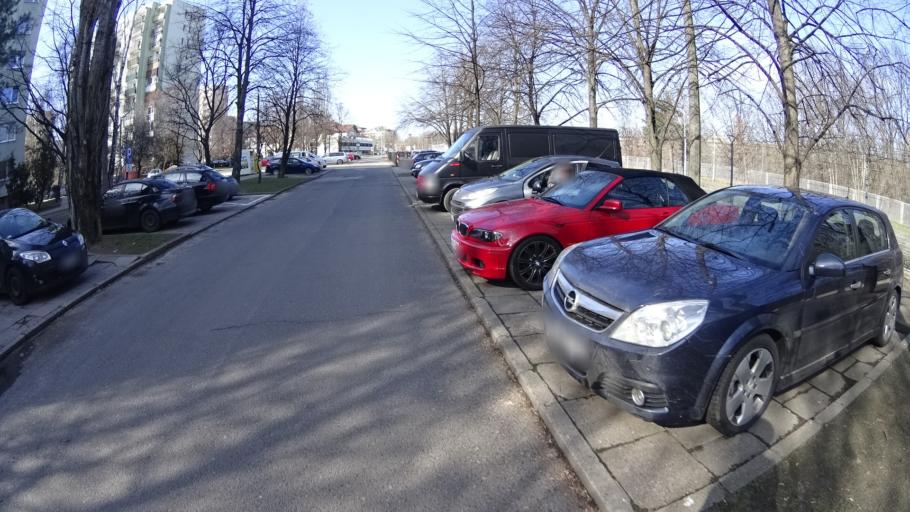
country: PL
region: Masovian Voivodeship
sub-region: Warszawa
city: Bemowo
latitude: 52.2528
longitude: 20.9293
